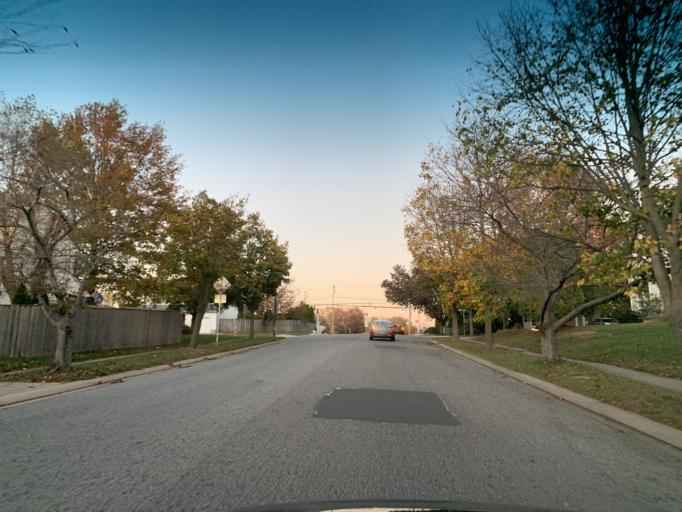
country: US
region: Maryland
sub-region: Harford County
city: South Bel Air
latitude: 39.5367
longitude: -76.3033
